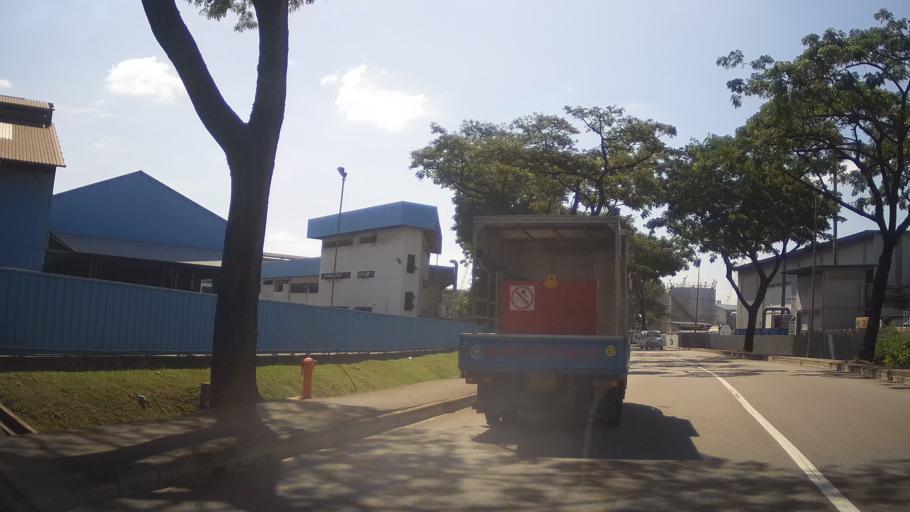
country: SG
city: Singapore
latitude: 1.3070
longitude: 103.6993
